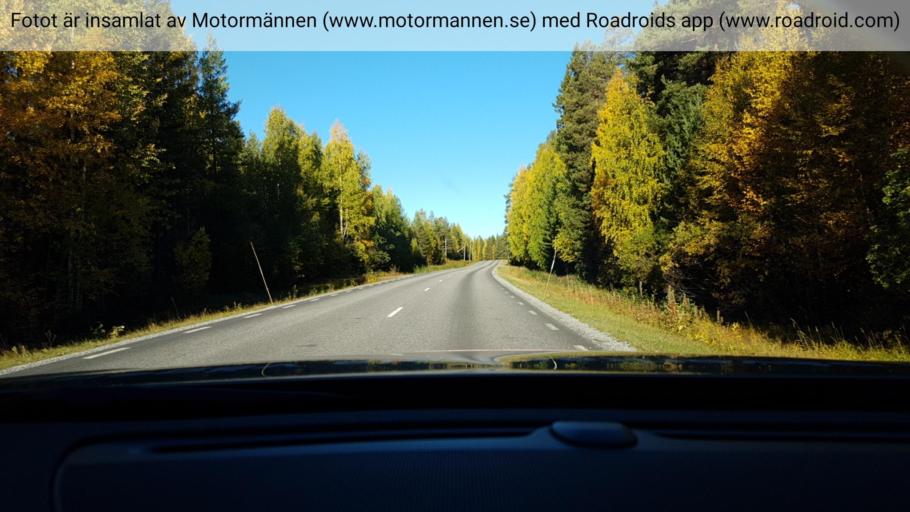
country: SE
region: Norrbotten
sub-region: Pitea Kommun
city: Roknas
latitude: 65.3544
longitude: 21.0868
